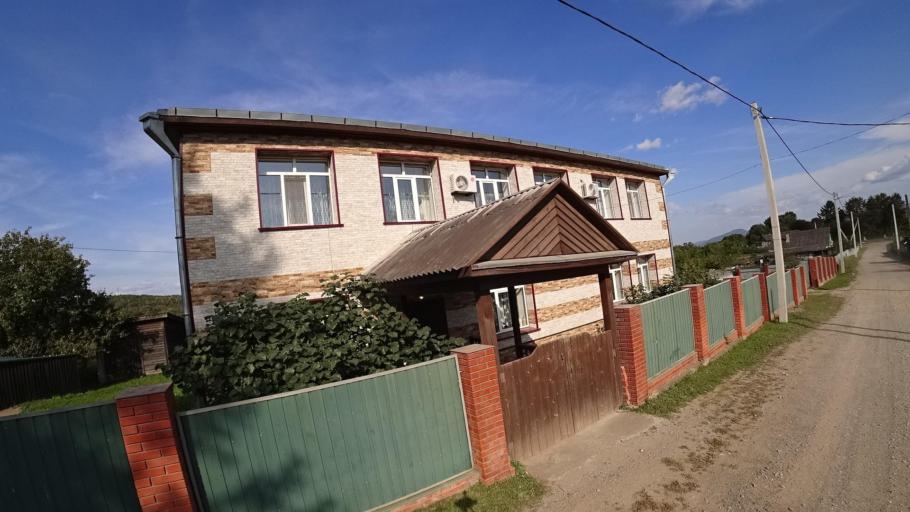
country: RU
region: Jewish Autonomous Oblast
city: Birakan
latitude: 49.0004
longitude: 131.7102
